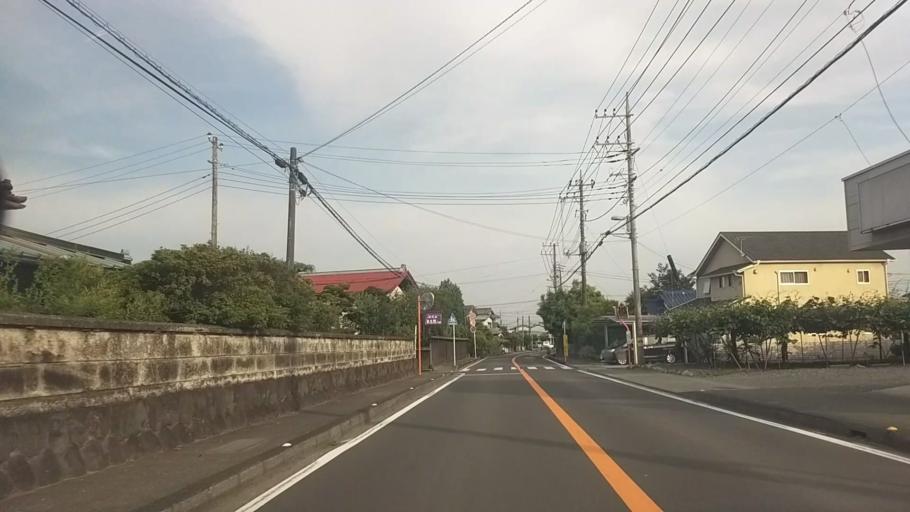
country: JP
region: Kanagawa
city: Odawara
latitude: 35.3538
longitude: 139.0918
